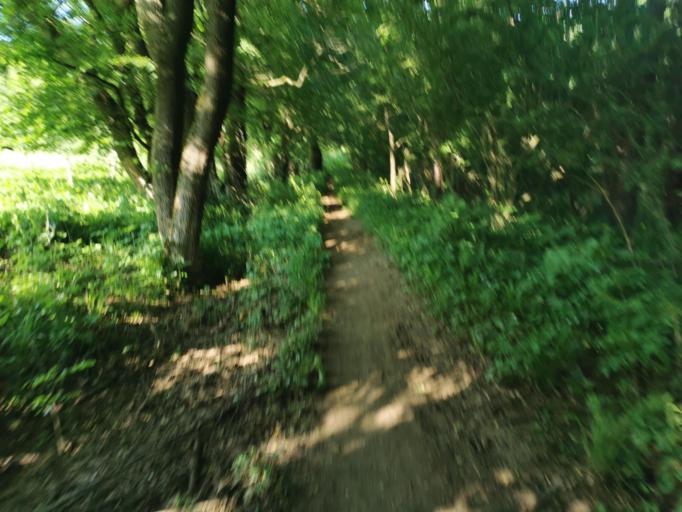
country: CZ
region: South Moravian
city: Knezdub
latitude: 48.8566
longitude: 17.3737
